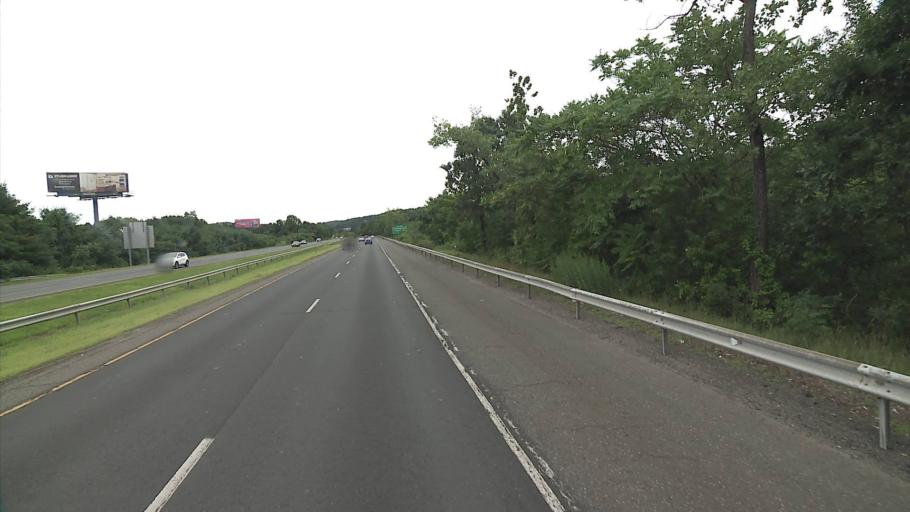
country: US
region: Connecticut
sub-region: New Haven County
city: Waterbury
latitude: 41.5735
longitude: -73.0540
